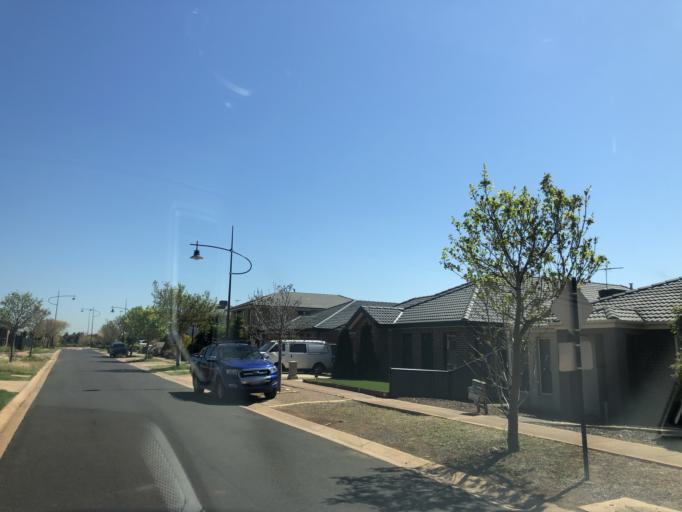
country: AU
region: Victoria
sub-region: Wyndham
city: Point Cook
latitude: -37.8962
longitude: 144.7327
